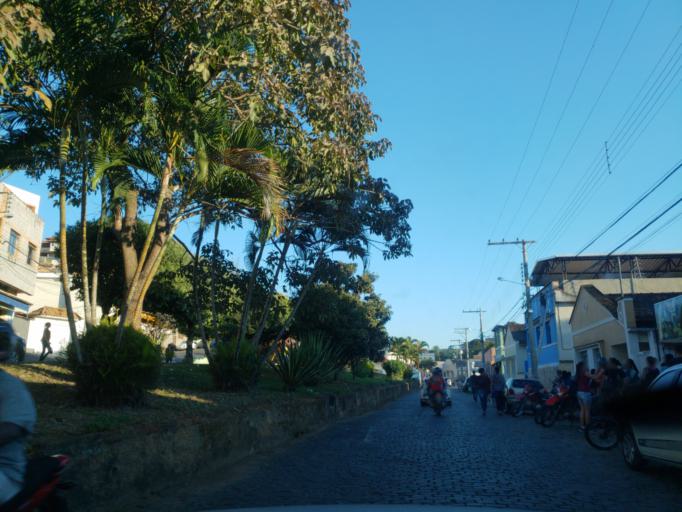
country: BR
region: Minas Gerais
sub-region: Sao Joao Nepomuceno
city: Sao Joao Nepomuceno
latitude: -21.5297
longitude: -43.0149
